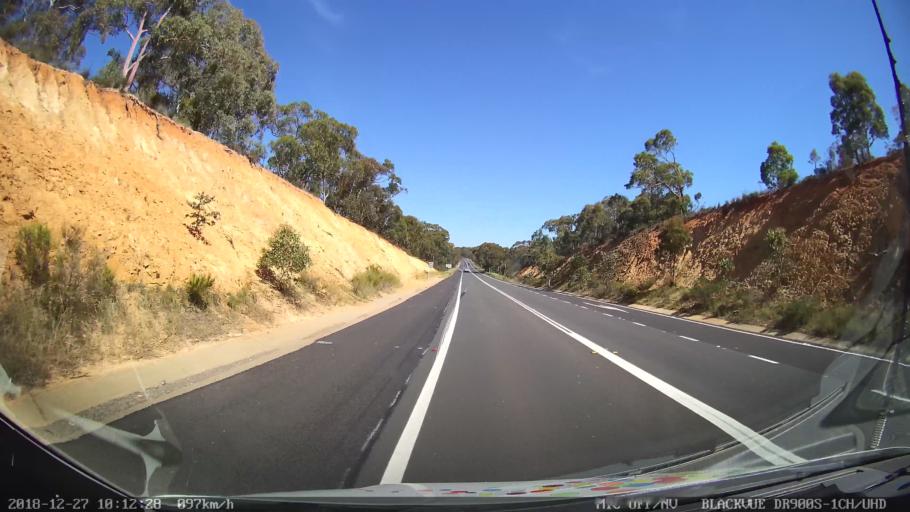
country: AU
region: New South Wales
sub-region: Bathurst Regional
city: Kelso
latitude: -33.4428
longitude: 149.7600
